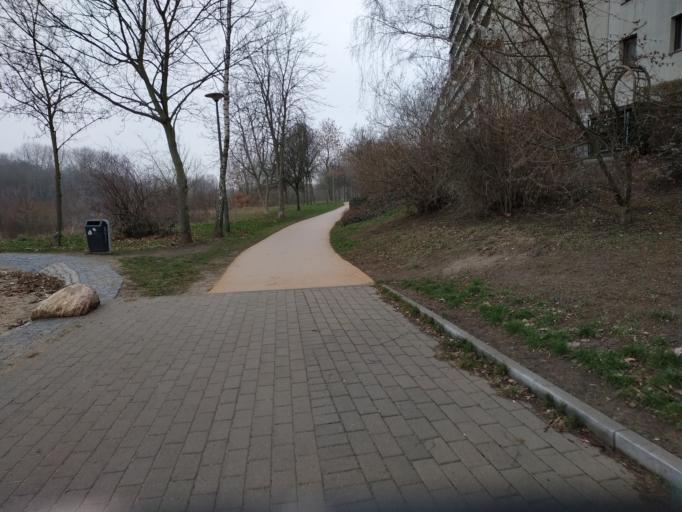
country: DE
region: Berlin
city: Kaulsdorf
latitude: 52.5352
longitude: 13.5879
